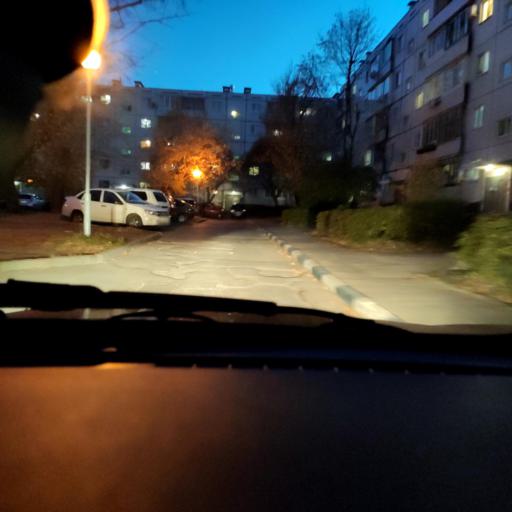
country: RU
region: Samara
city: Tol'yatti
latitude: 53.5322
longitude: 49.2935
